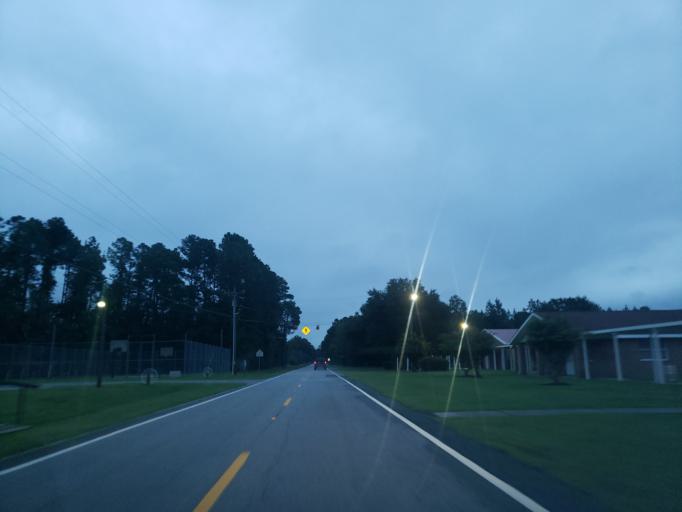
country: US
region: Georgia
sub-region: Chatham County
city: Bloomingdale
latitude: 32.0915
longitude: -81.3430
